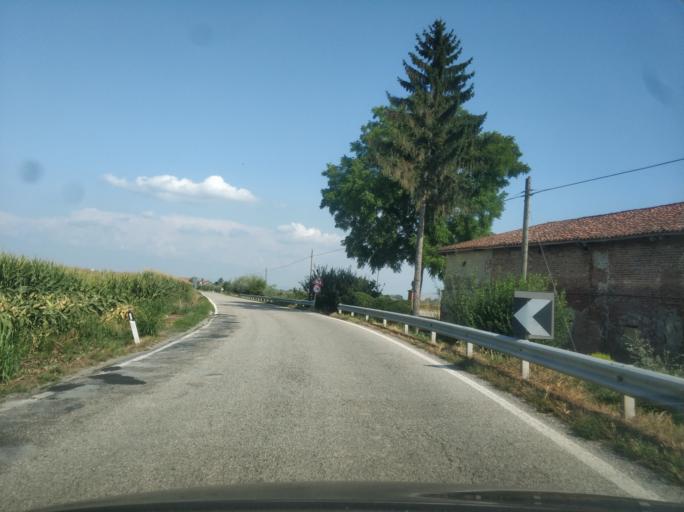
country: IT
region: Piedmont
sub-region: Provincia di Cuneo
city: Centallo
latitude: 44.5335
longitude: 7.6285
